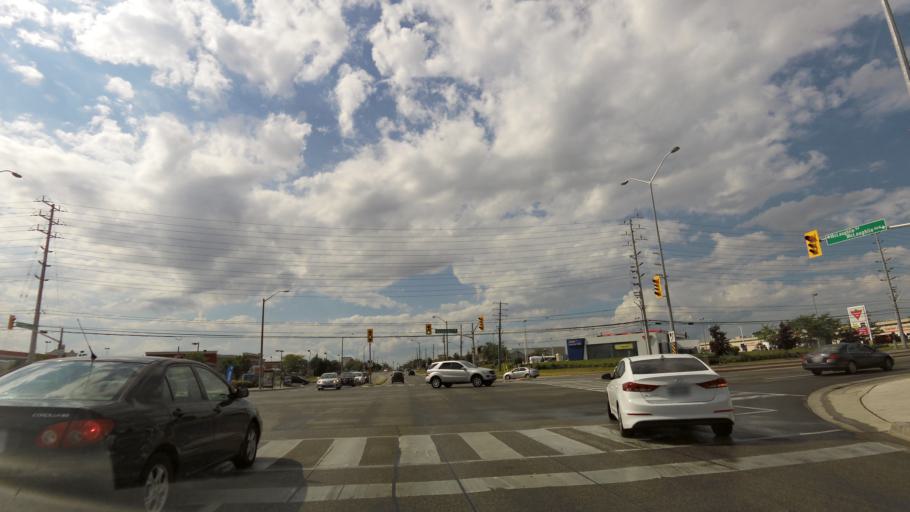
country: CA
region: Ontario
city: Brampton
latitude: 43.6958
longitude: -79.7972
